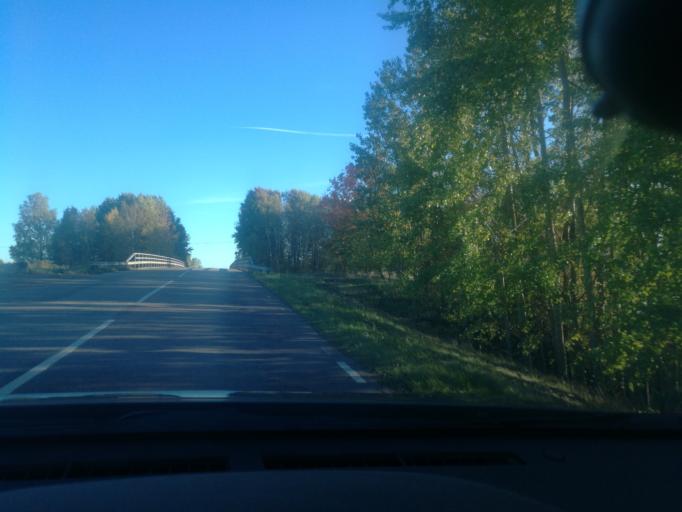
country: SE
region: Vaestmanland
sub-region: Kopings Kommun
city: Koping
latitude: 59.5706
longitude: 16.0898
